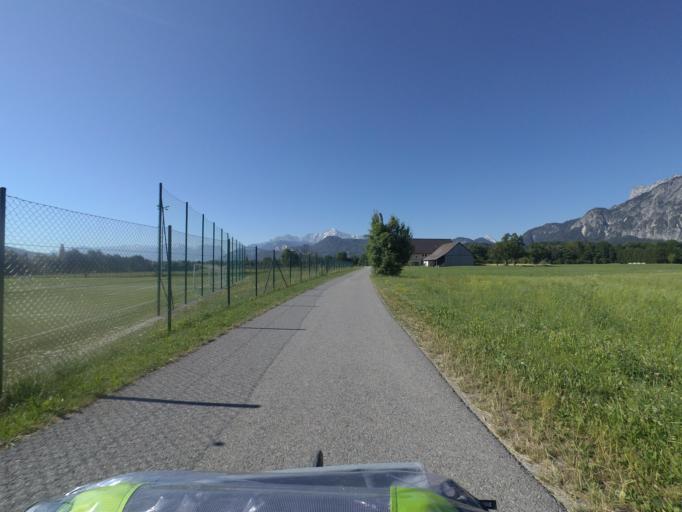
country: AT
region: Salzburg
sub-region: Politischer Bezirk Salzburg-Umgebung
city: Anif
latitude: 47.7405
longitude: 13.0622
